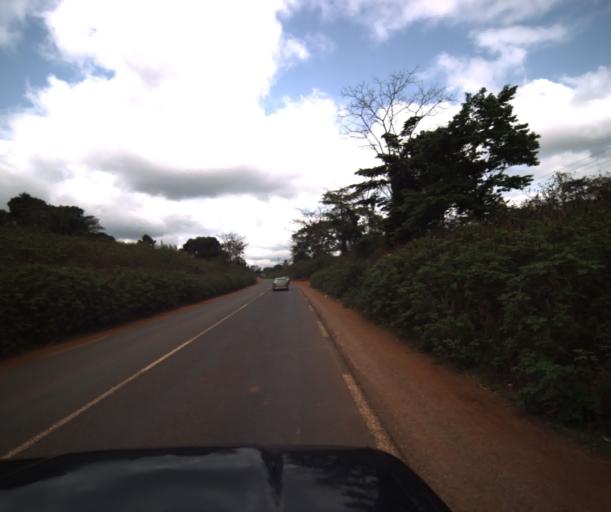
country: CM
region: Centre
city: Mbankomo
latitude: 3.7899
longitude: 11.4366
